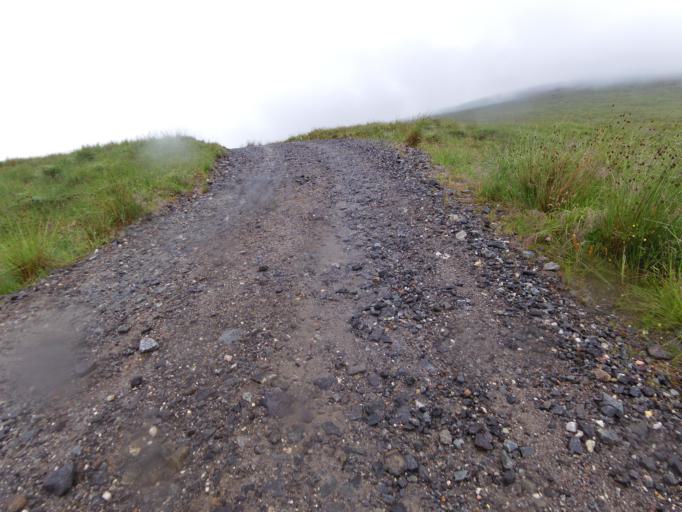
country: GB
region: Scotland
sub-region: Highland
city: Spean Bridge
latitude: 56.7689
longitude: -4.6762
